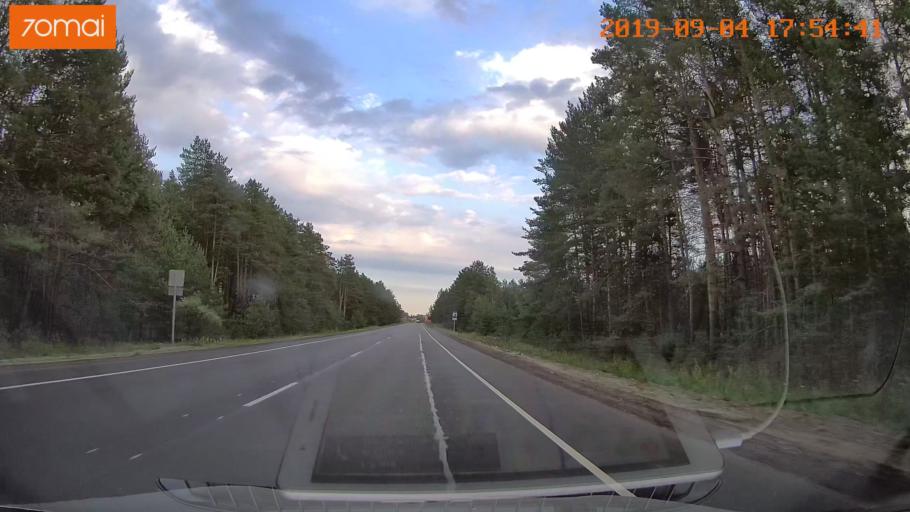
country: RU
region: Moskovskaya
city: Imeni Tsyurupy
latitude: 55.5092
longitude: 38.7514
